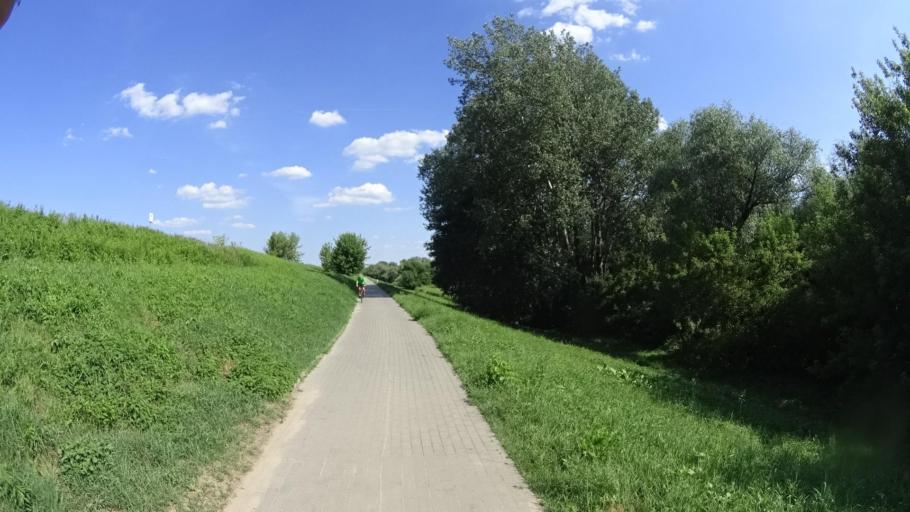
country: PL
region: Masovian Voivodeship
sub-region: Warszawa
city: Bialoleka
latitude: 52.3064
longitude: 20.9575
